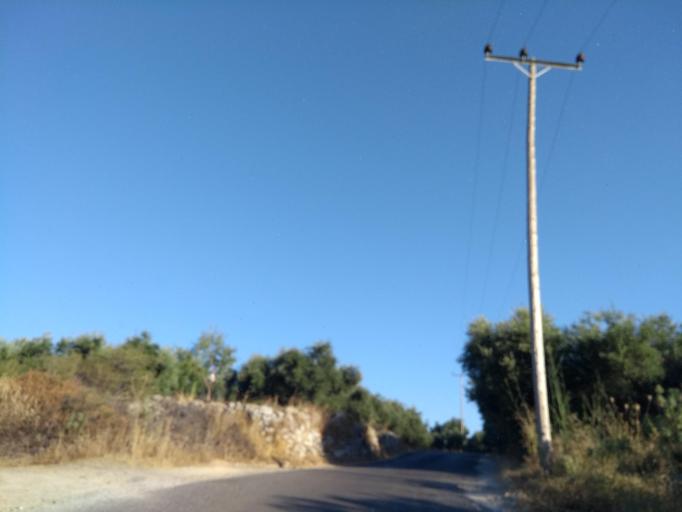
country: GR
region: Crete
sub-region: Nomos Chanias
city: Kalivai
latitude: 35.4352
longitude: 24.1750
